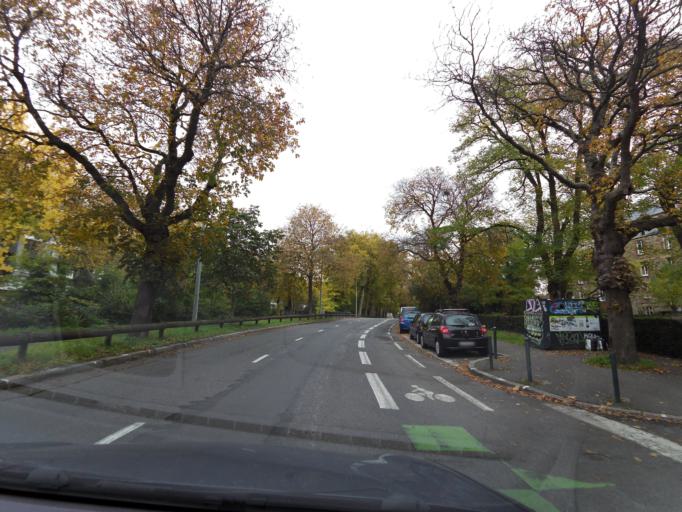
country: FR
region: Brittany
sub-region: Departement d'Ille-et-Vilaine
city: Rennes
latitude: 48.1184
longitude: -1.6852
